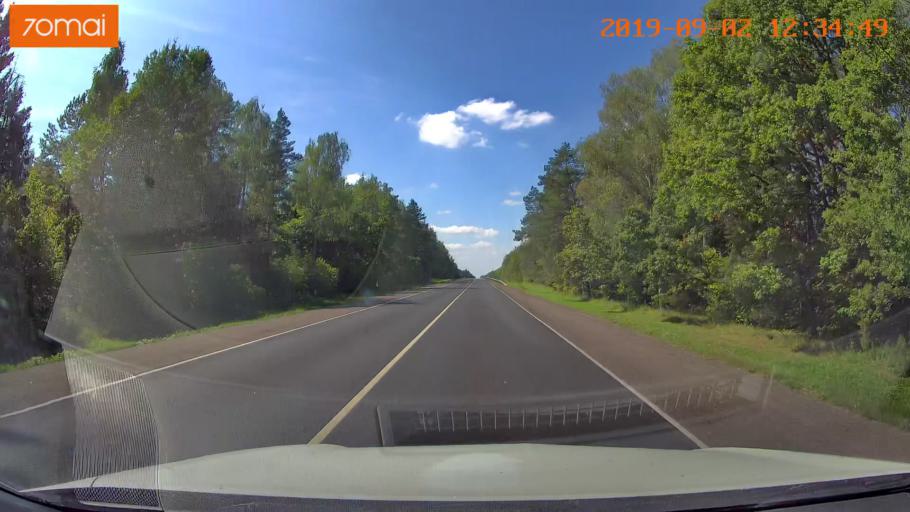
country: RU
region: Smolensk
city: Shumyachi
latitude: 53.8075
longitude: 32.3952
